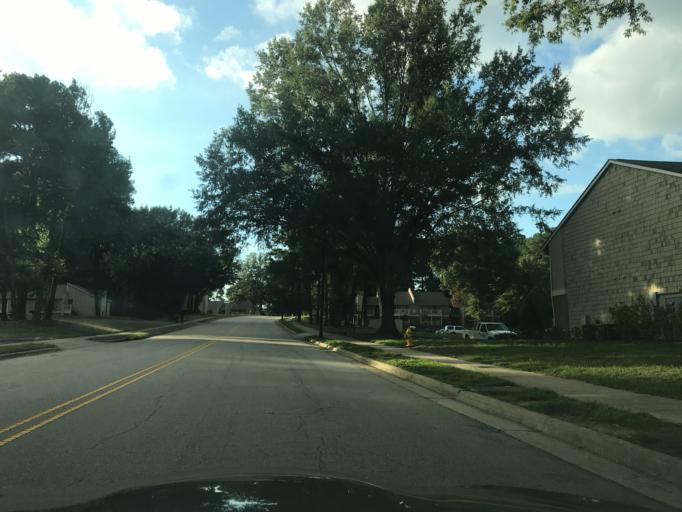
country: US
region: North Carolina
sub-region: Wake County
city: West Raleigh
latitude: 35.8640
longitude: -78.6307
